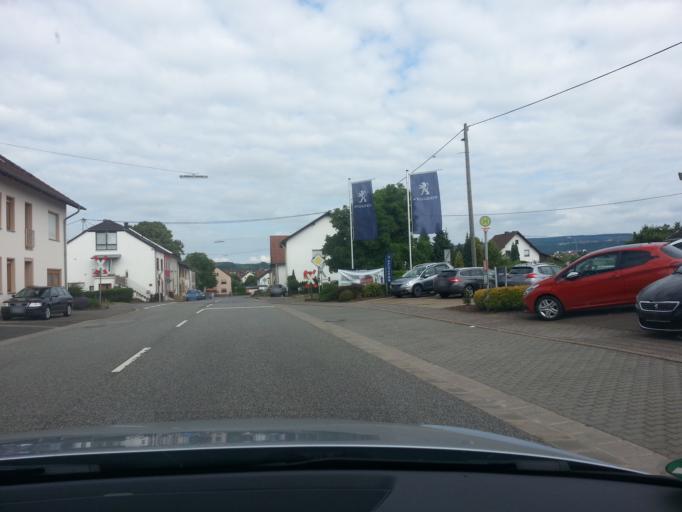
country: DE
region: Saarland
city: Losheim
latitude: 49.5040
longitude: 6.7537
